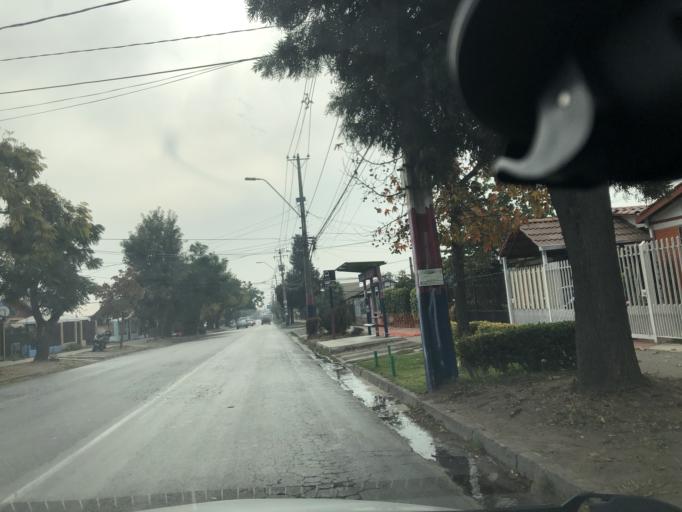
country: CL
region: Santiago Metropolitan
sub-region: Provincia de Cordillera
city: Puente Alto
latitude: -33.5757
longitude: -70.5704
